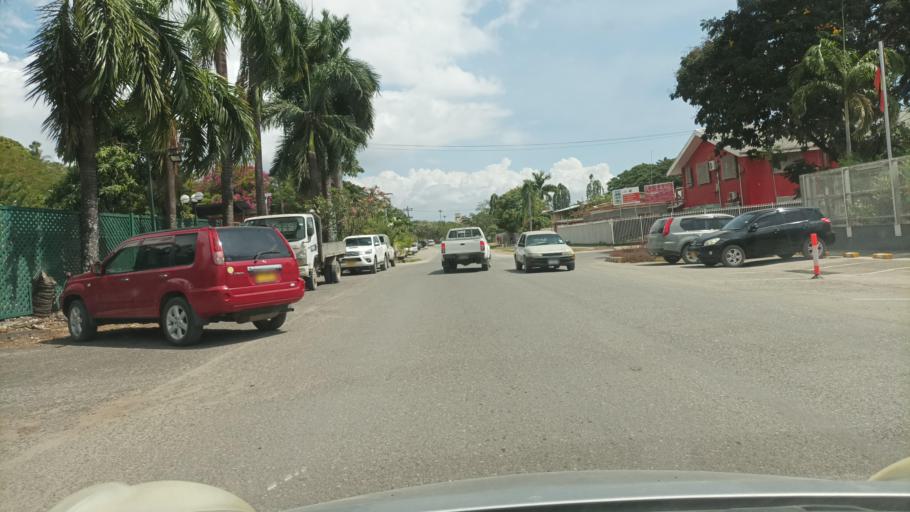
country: SB
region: Guadalcanal
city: Honiara
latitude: -9.4321
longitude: 159.9529
